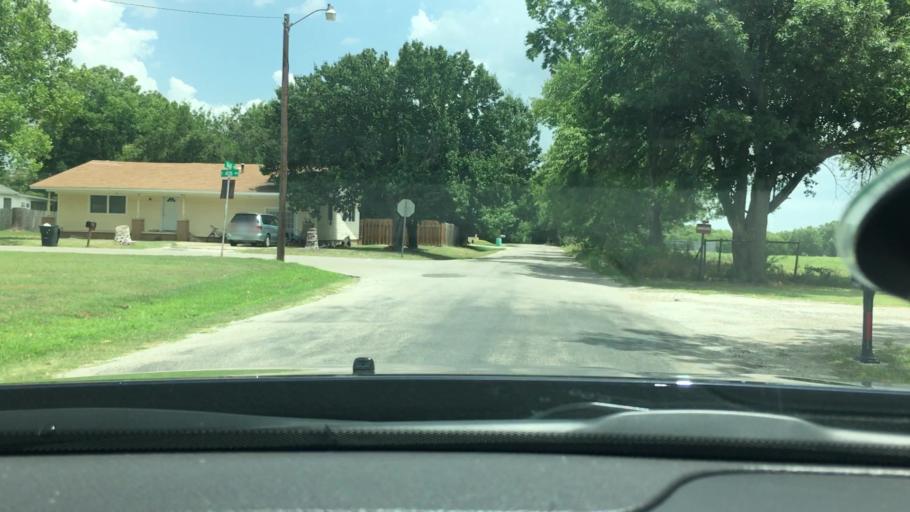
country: US
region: Oklahoma
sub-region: Love County
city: Marietta
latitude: 33.9296
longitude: -97.1212
